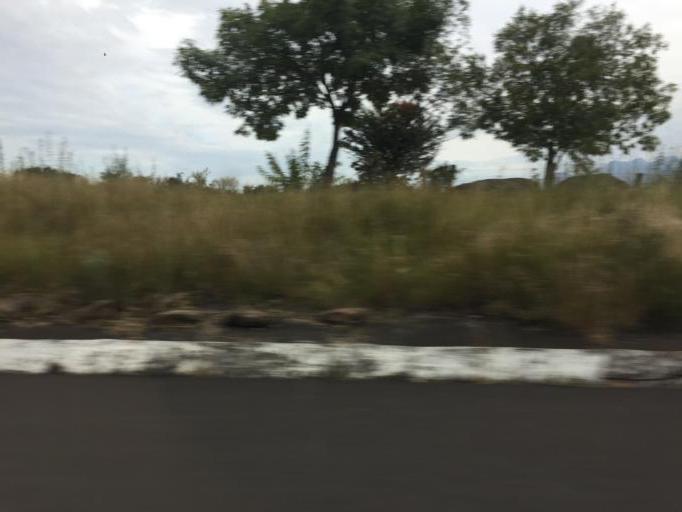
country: MX
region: Mexico
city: Huaniqueo de Morales
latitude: 19.8847
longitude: -101.4866
